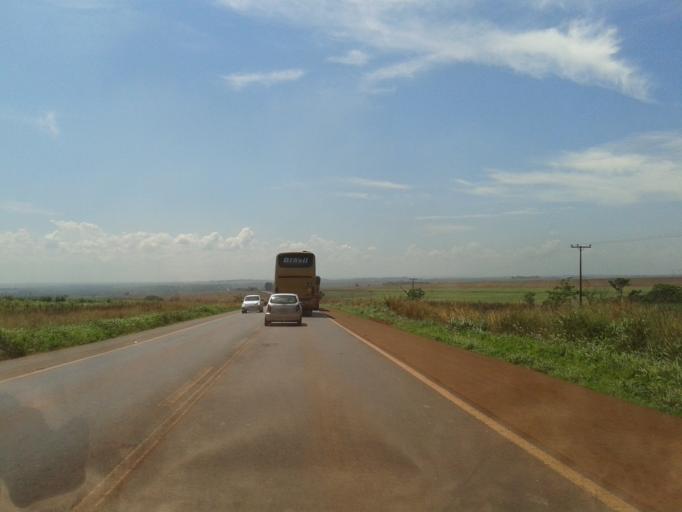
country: BR
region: Goias
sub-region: Santa Helena De Goias
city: Santa Helena de Goias
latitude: -18.0223
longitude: -50.3326
